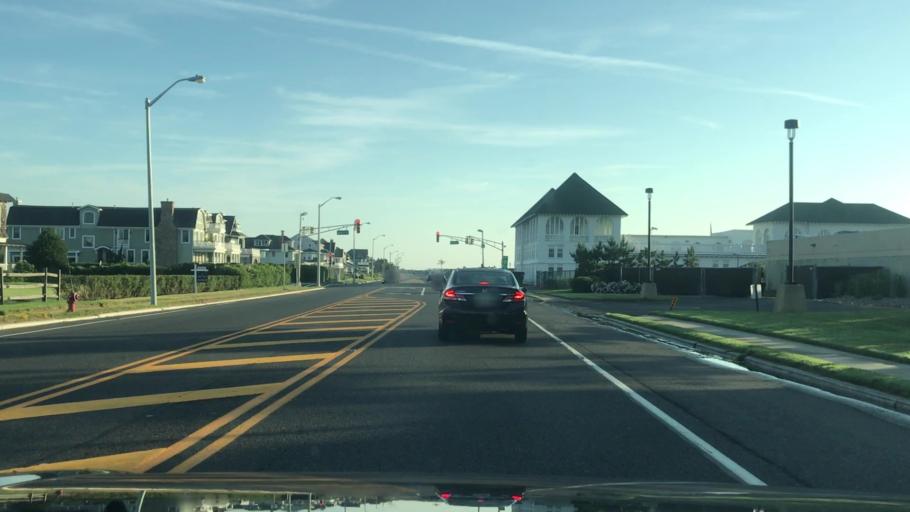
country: US
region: New Jersey
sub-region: Monmouth County
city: Monmouth Beach
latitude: 40.3311
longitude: -73.9749
